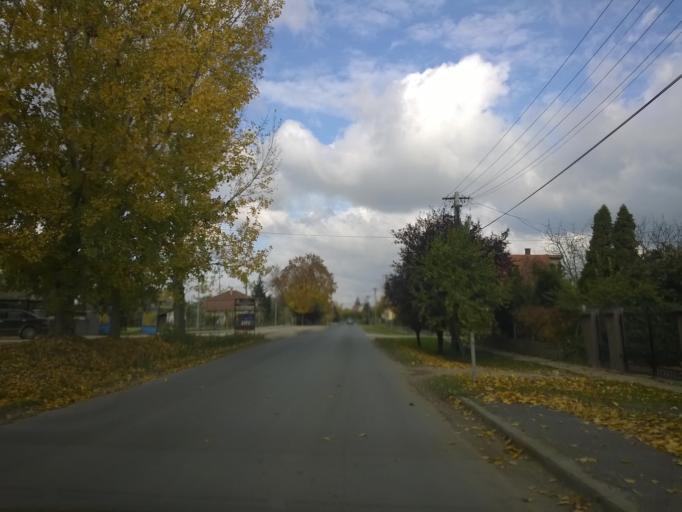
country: HU
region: Pest
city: Rackeve
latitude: 47.1557
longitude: 18.9555
